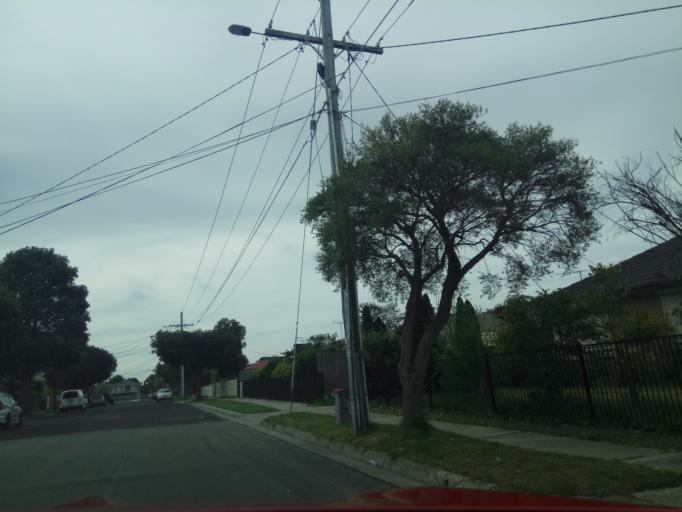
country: AU
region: Victoria
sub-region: Greater Dandenong
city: Springvale South
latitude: -37.9630
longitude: 145.1398
